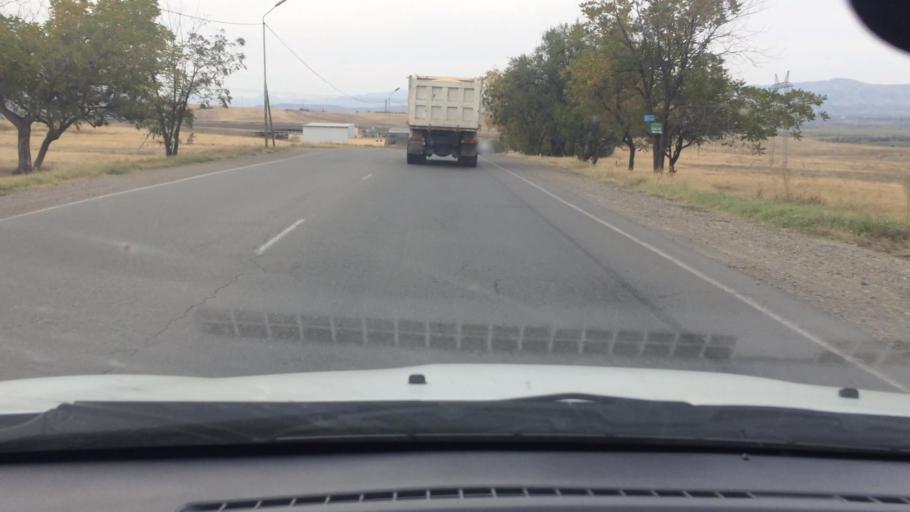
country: GE
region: Kvemo Kartli
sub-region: Marneuli
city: Marneuli
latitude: 41.5166
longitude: 44.7843
